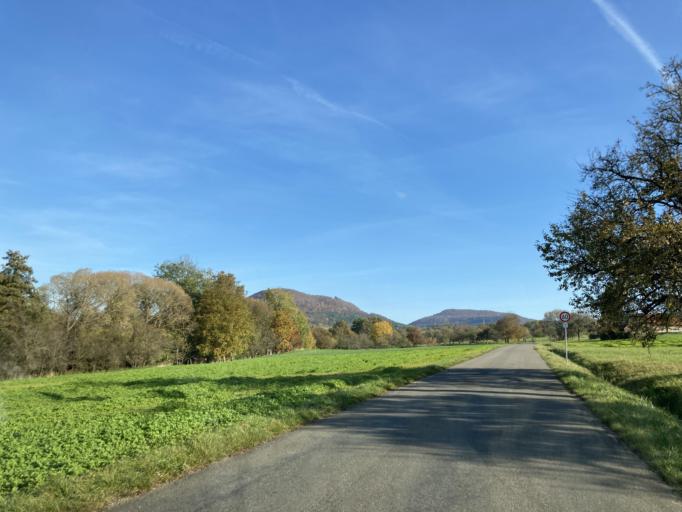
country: DE
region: Baden-Wuerttemberg
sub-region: Tuebingen Region
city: Mossingen
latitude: 48.4043
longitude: 9.0725
